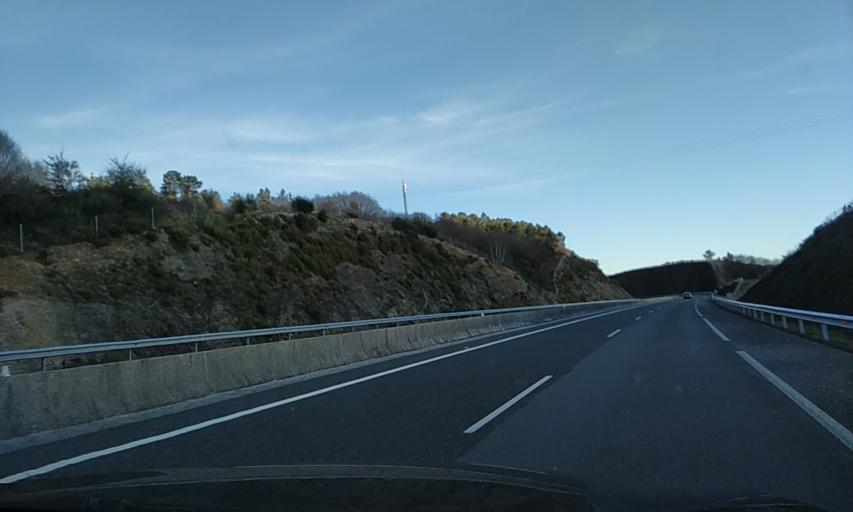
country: ES
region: Galicia
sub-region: Provincia de Pontevedra
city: Dozon
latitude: 42.5942
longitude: -8.0857
